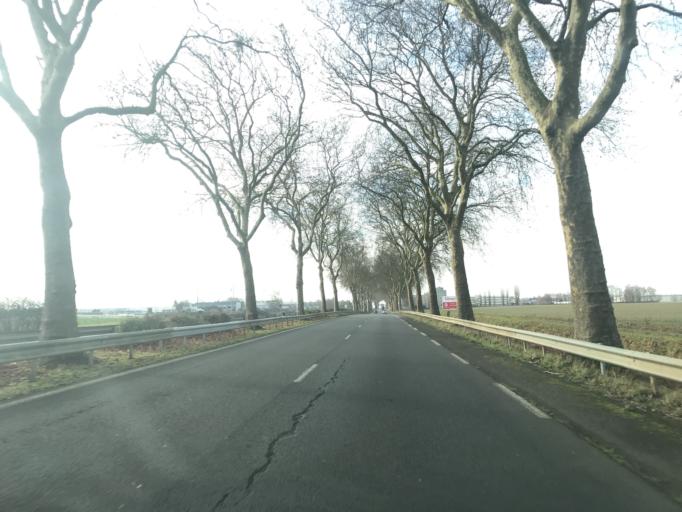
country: FR
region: Poitou-Charentes
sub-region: Departement des Deux-Sevres
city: Chauray
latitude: 46.3462
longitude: -0.3634
